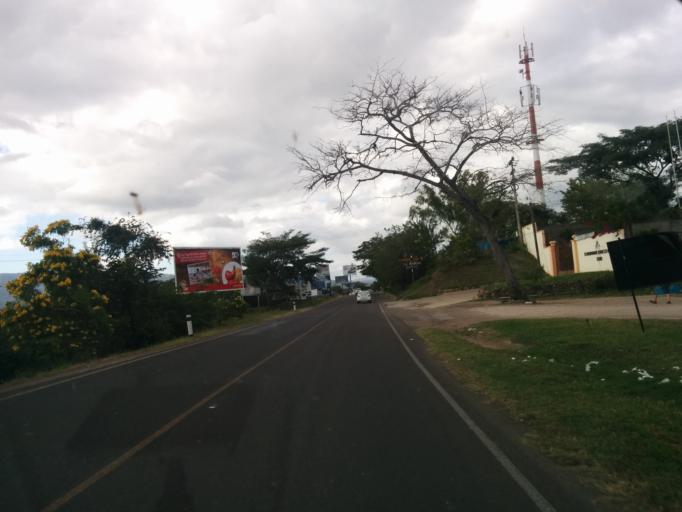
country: NI
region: Esteli
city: Esteli
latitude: 13.0616
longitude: -86.3453
